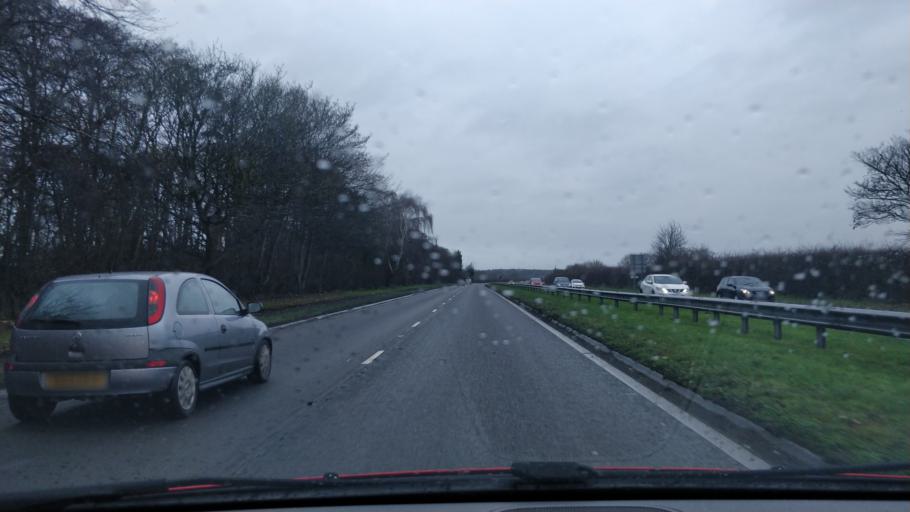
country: GB
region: England
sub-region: Sefton
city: Formby
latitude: 53.5693
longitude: -3.0483
